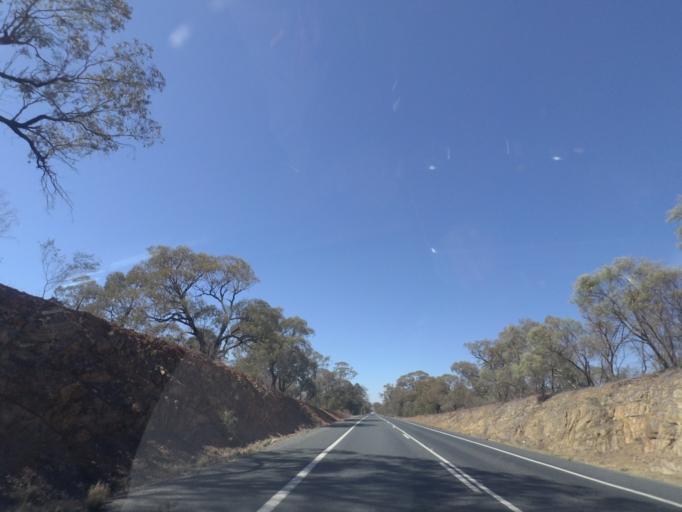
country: AU
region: New South Wales
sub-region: Bland
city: West Wyalong
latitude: -34.1673
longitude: 147.1157
